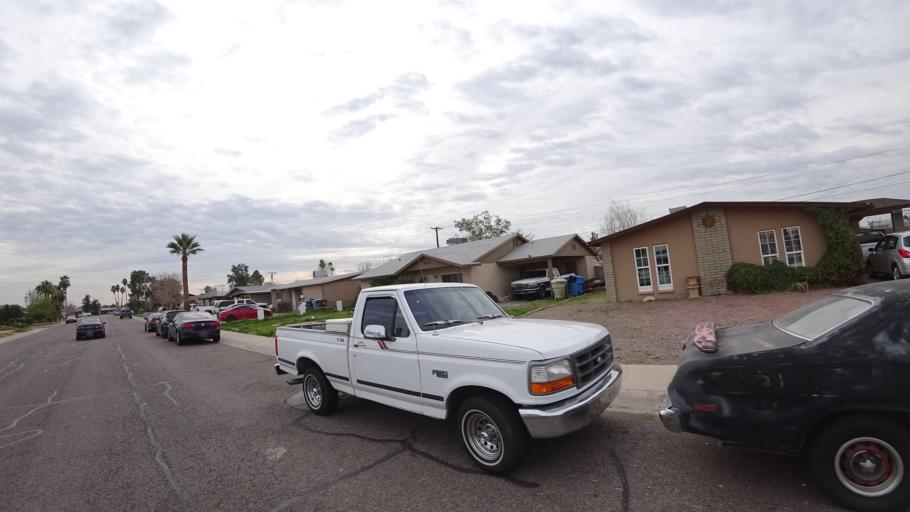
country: US
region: Arizona
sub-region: Maricopa County
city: Glendale
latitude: 33.6224
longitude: -112.1204
